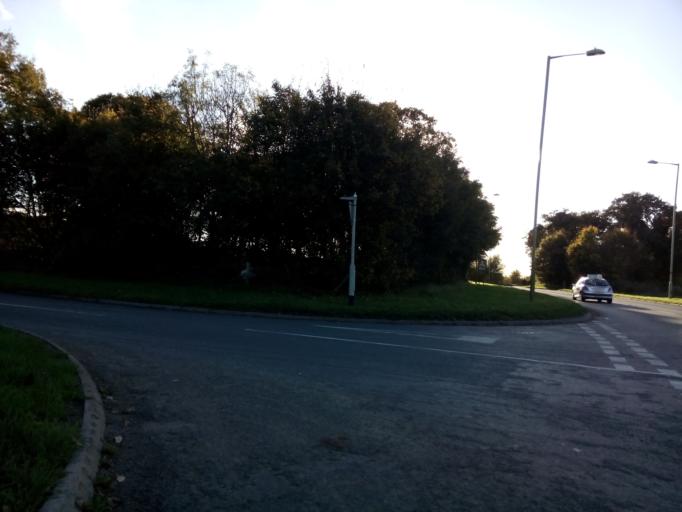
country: GB
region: England
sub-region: Suffolk
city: Kesgrave
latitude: 52.0482
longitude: 1.2777
